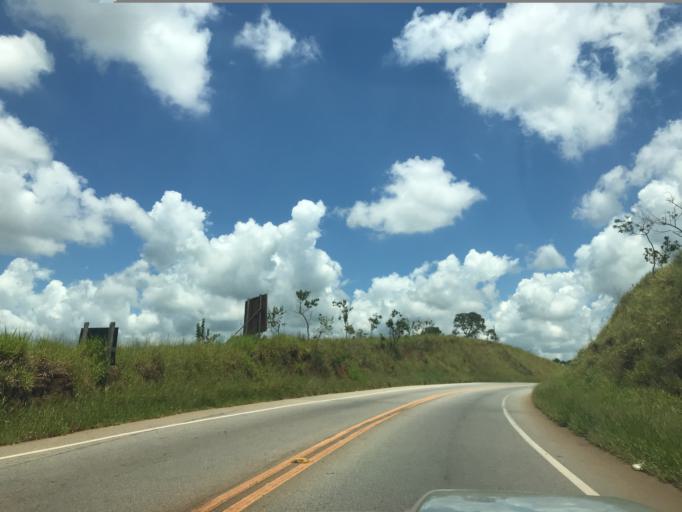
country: BR
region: Minas Gerais
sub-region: Tres Coracoes
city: Tres Coracoes
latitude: -21.6585
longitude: -45.2983
